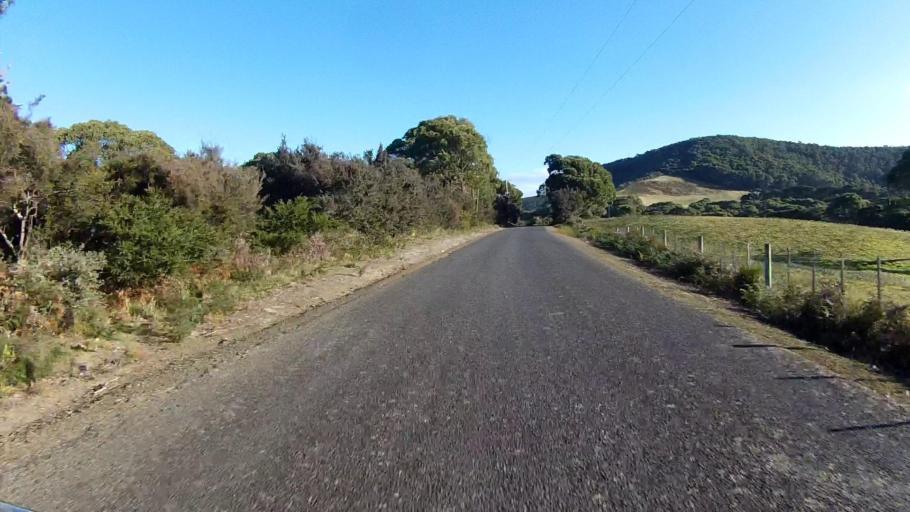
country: AU
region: Tasmania
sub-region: Clarence
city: Sandford
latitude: -43.1833
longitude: 147.8523
